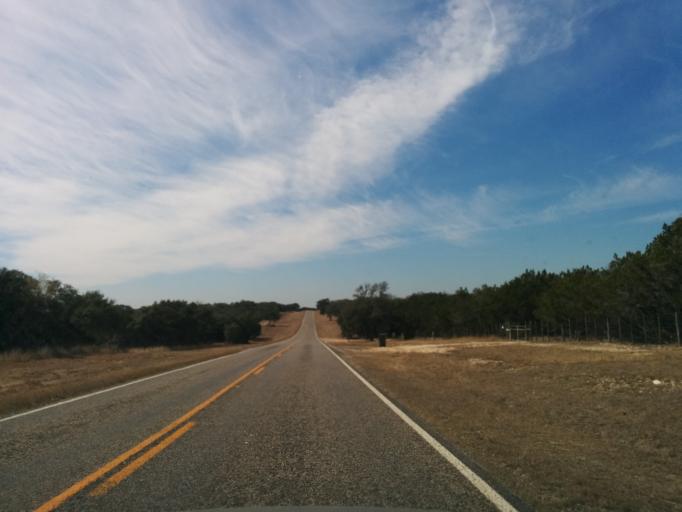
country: US
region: Texas
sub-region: Blanco County
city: Blanco
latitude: 29.9565
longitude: -98.5447
